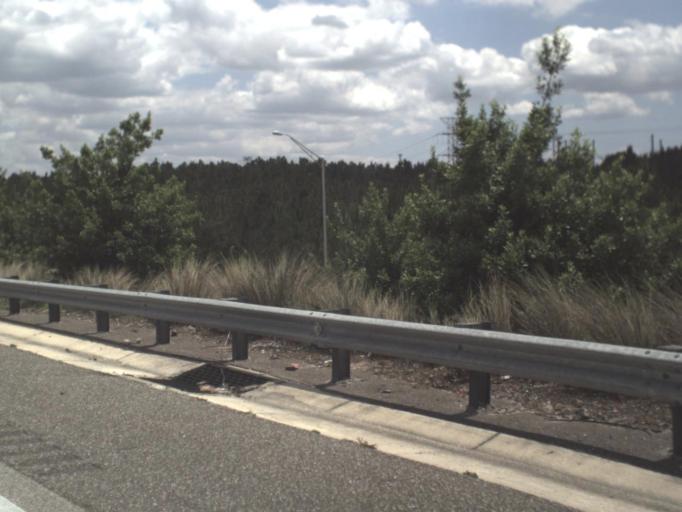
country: US
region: Florida
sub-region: Duval County
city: Jacksonville Beach
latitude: 30.2672
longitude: -81.5203
